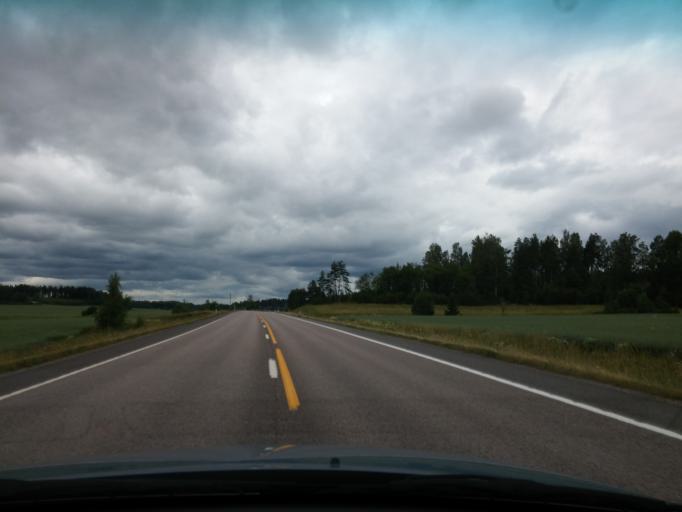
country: FI
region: Uusimaa
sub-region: Porvoo
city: Askola
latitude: 60.4768
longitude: 25.5673
